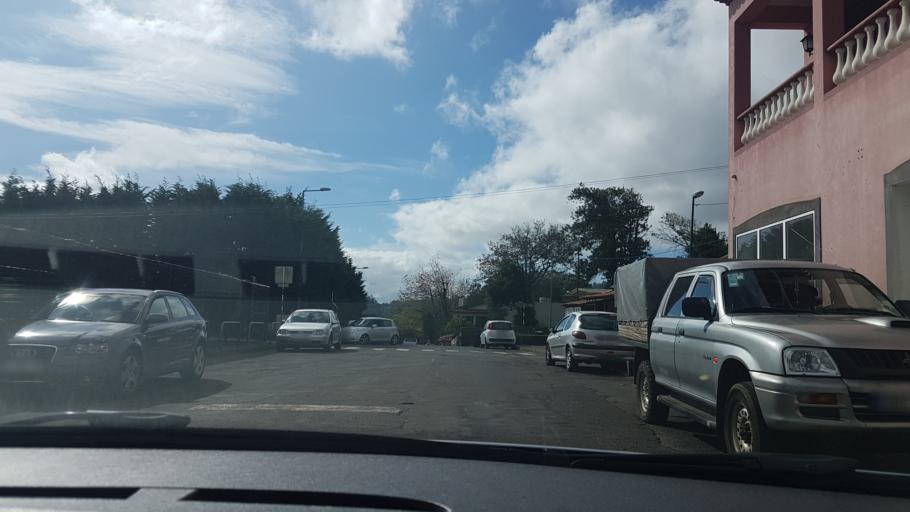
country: PT
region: Madeira
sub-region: Santa Cruz
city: Santa Cruz
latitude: 32.7259
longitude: -16.8204
